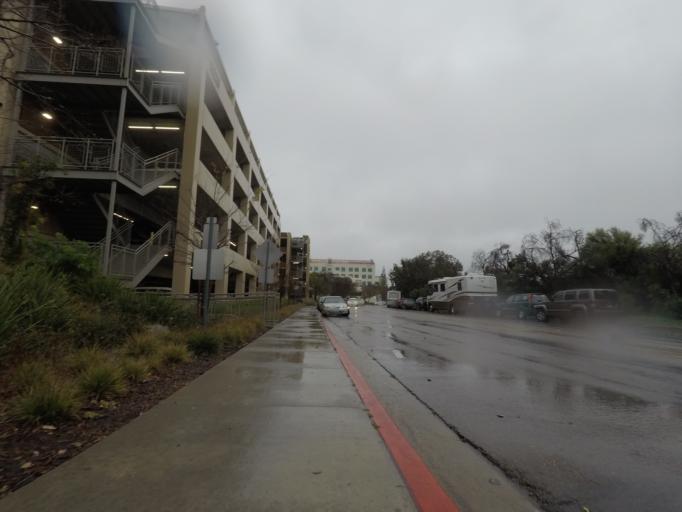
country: US
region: California
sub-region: San Diego County
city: San Diego
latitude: 32.7969
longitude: -117.1537
